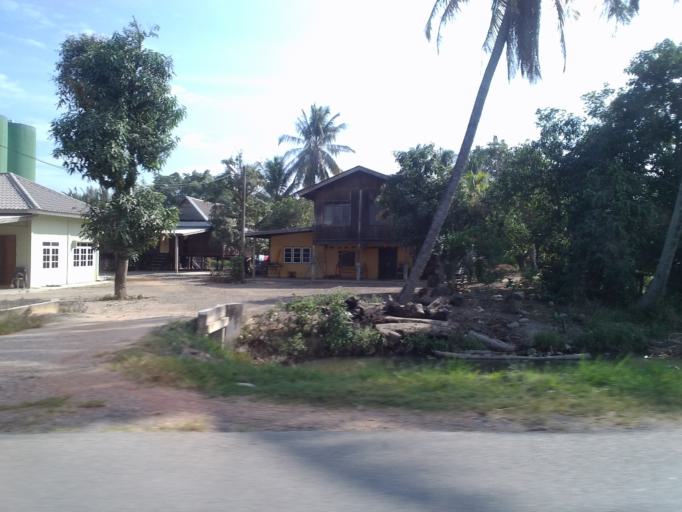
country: MY
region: Kedah
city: Gurun
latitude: 5.9607
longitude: 100.4050
